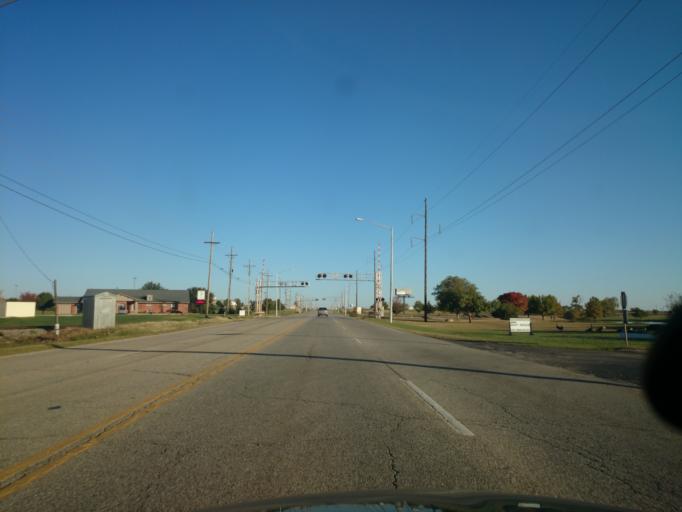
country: US
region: Oklahoma
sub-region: Payne County
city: Stillwater
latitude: 36.1526
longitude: -97.0517
